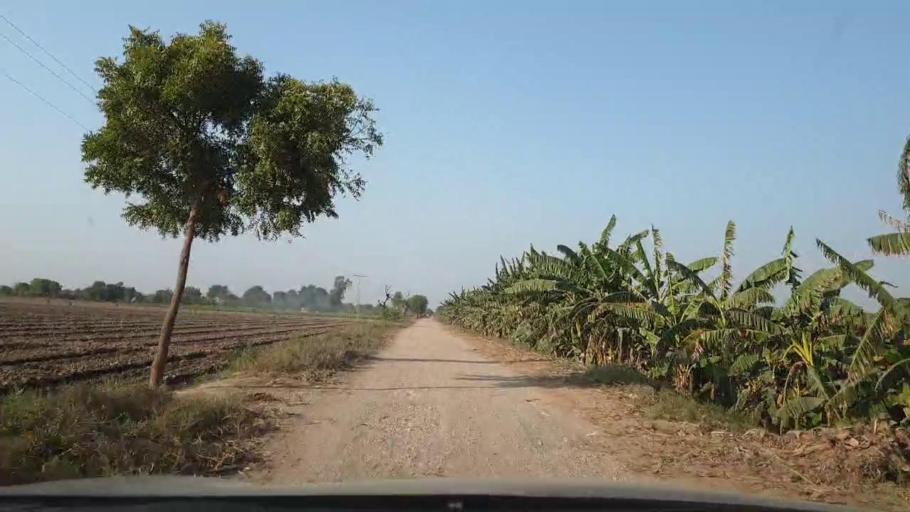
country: PK
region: Sindh
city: Tando Allahyar
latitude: 25.5761
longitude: 68.7801
